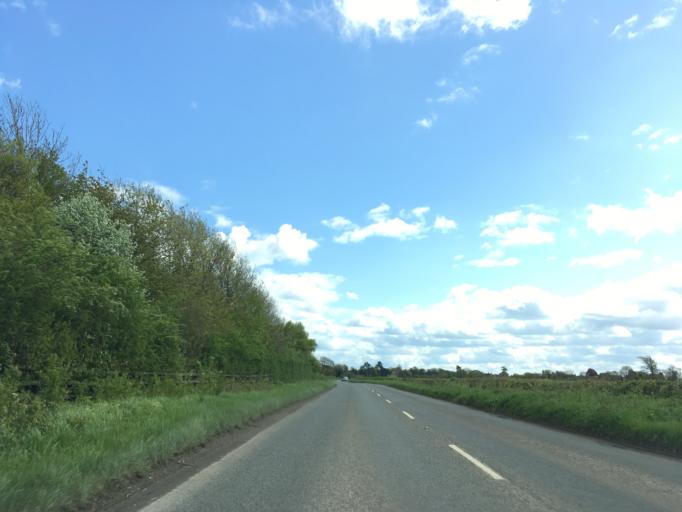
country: GB
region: England
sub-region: South Gloucestershire
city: Wickwar
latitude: 51.6047
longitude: -2.4087
